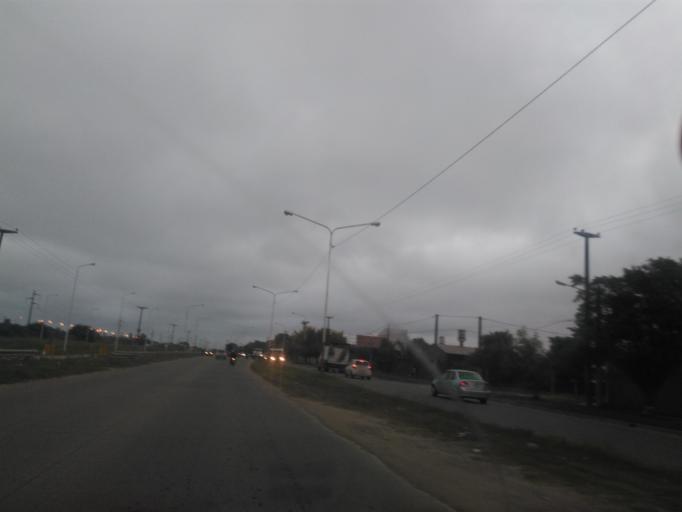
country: AR
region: Chaco
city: Resistencia
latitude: -27.4660
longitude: -59.0129
